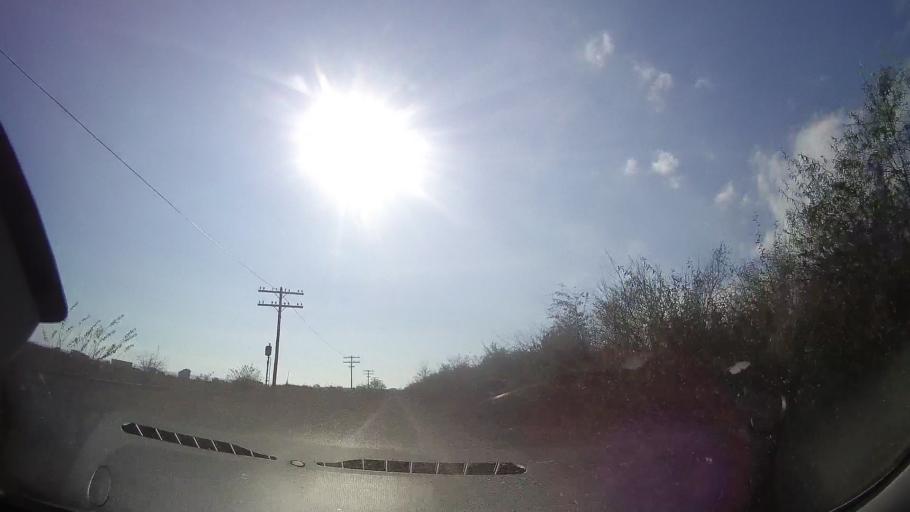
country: RO
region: Constanta
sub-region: Comuna Costinesti
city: Costinesti
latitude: 43.9724
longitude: 28.6434
